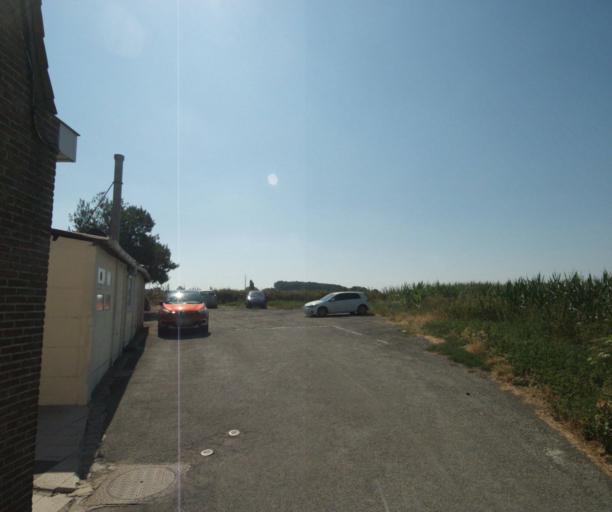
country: FR
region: Nord-Pas-de-Calais
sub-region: Departement du Nord
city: Bousbecque
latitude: 50.7727
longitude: 3.0920
